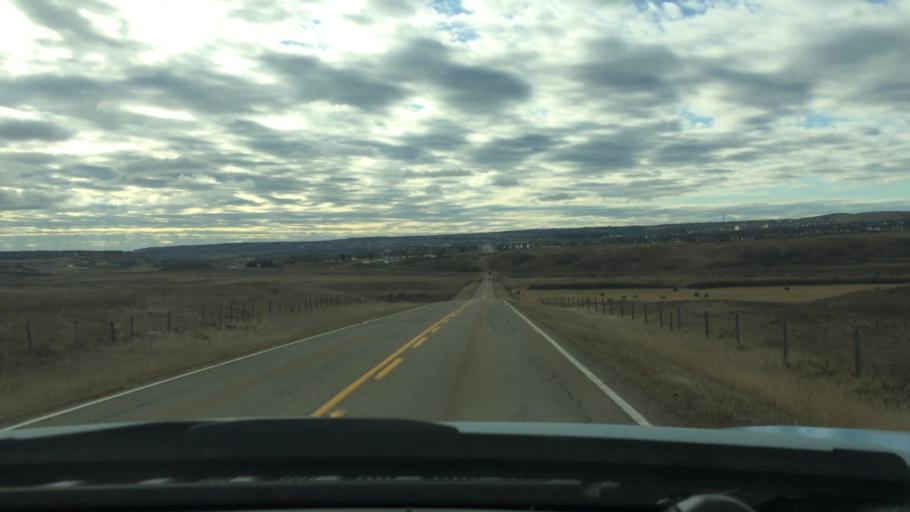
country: CA
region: Alberta
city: Airdrie
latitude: 51.1962
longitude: -114.1413
